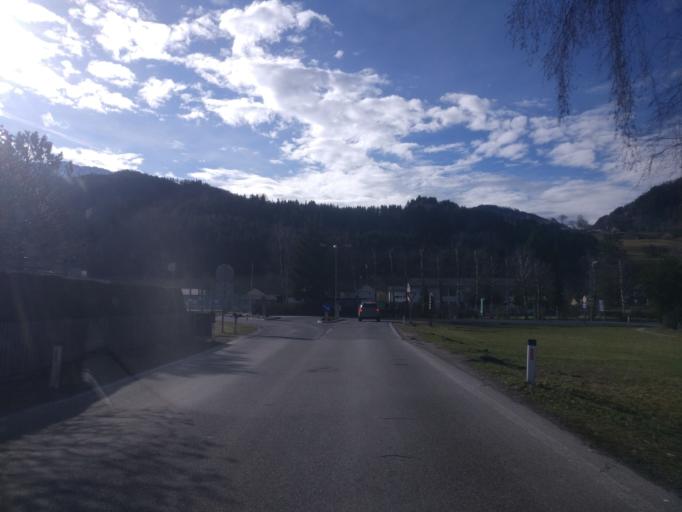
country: AT
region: Styria
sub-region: Politischer Bezirk Liezen
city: Sankt Gallen
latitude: 47.6857
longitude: 14.6188
